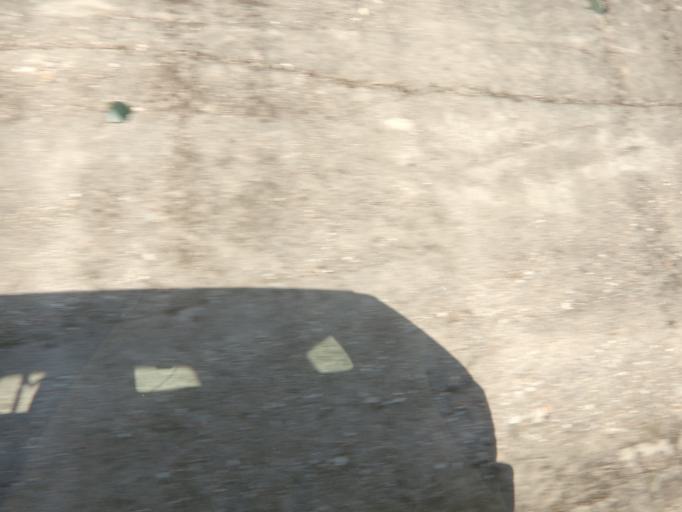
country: PT
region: Vila Real
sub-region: Mesao Frio
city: Mesao Frio
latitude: 41.1933
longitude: -7.8453
